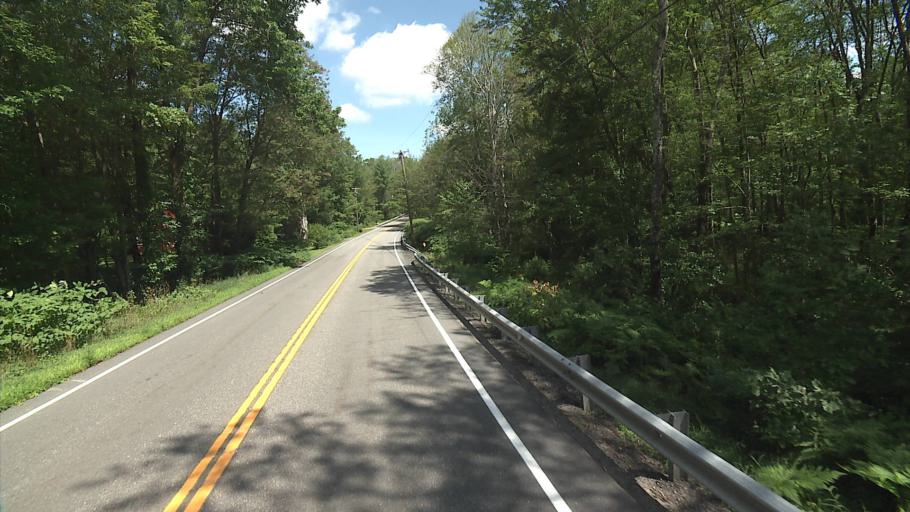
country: US
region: Massachusetts
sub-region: Worcester County
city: Southbridge
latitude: 42.0200
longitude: -72.0756
